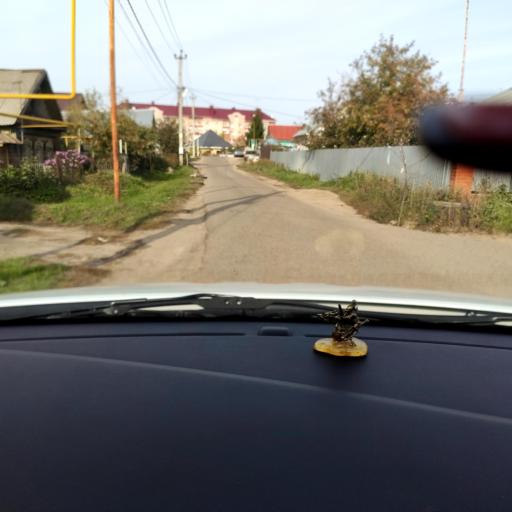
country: RU
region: Tatarstan
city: Vysokaya Gora
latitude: 55.9079
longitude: 49.3011
